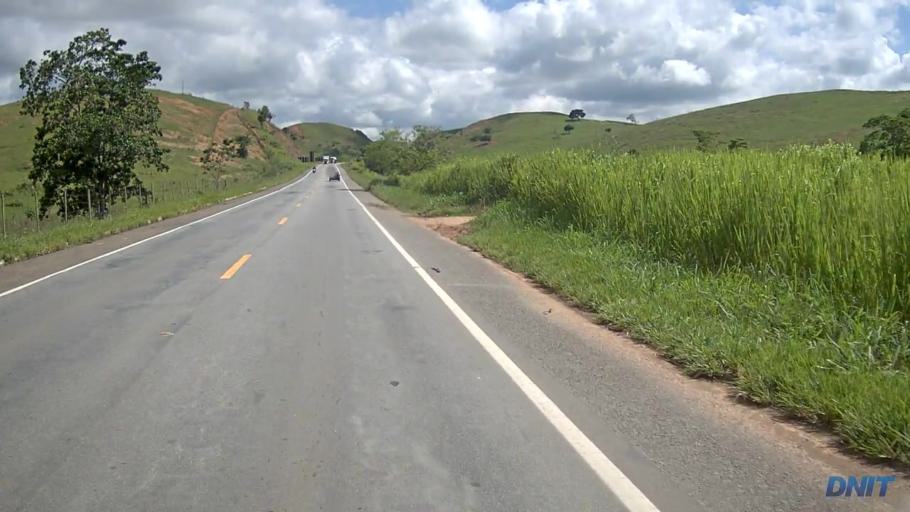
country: BR
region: Minas Gerais
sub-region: Belo Oriente
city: Belo Oriente
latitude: -19.1297
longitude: -42.2134
